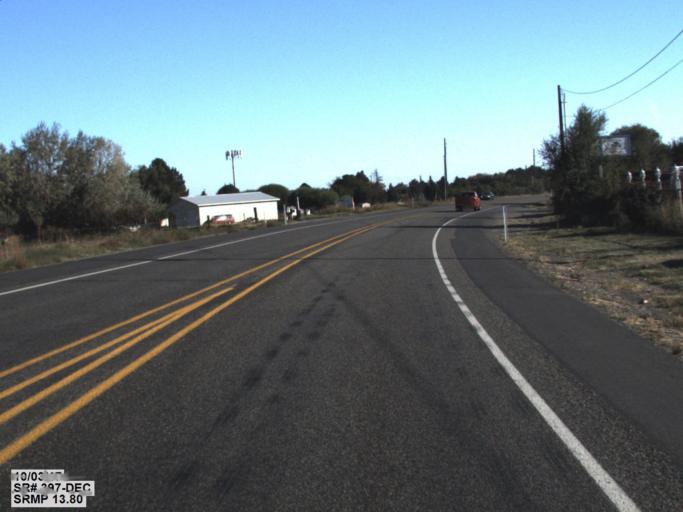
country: US
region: Washington
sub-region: Benton County
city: Finley
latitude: 46.1727
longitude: -119.0532
